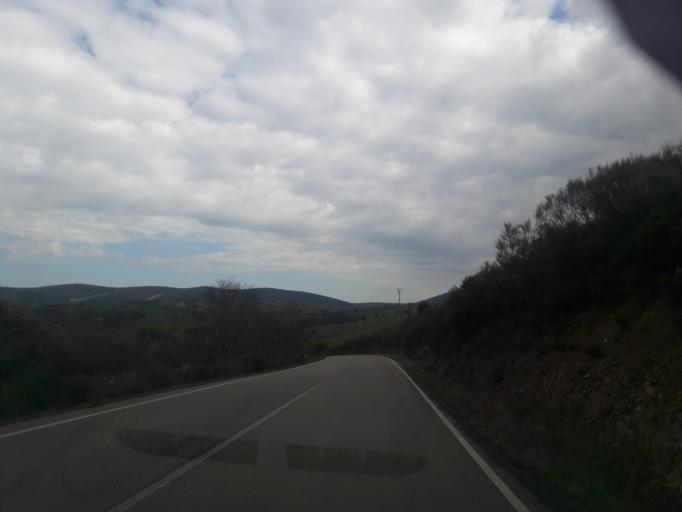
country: ES
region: Castille and Leon
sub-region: Provincia de Salamanca
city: Serradilla del Arroyo
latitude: 40.5104
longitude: -6.3623
